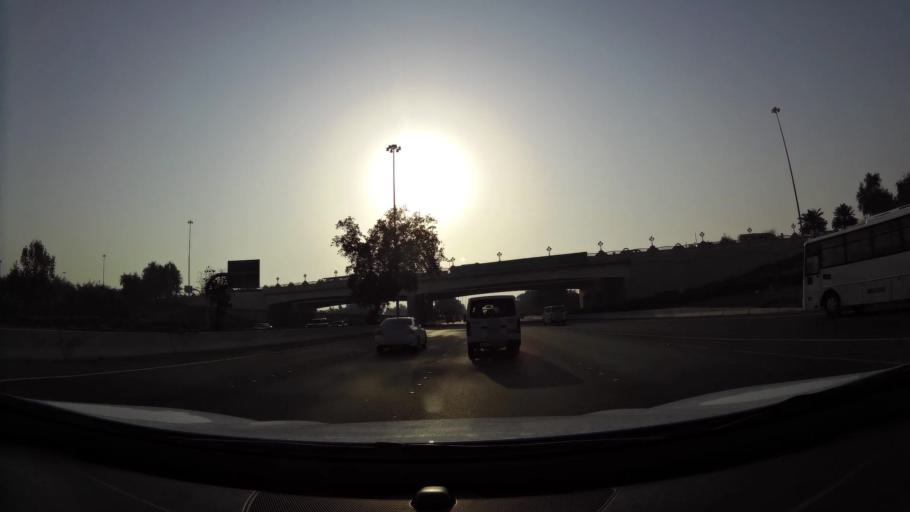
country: AE
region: Abu Dhabi
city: Abu Dhabi
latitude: 24.4147
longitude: 54.5031
